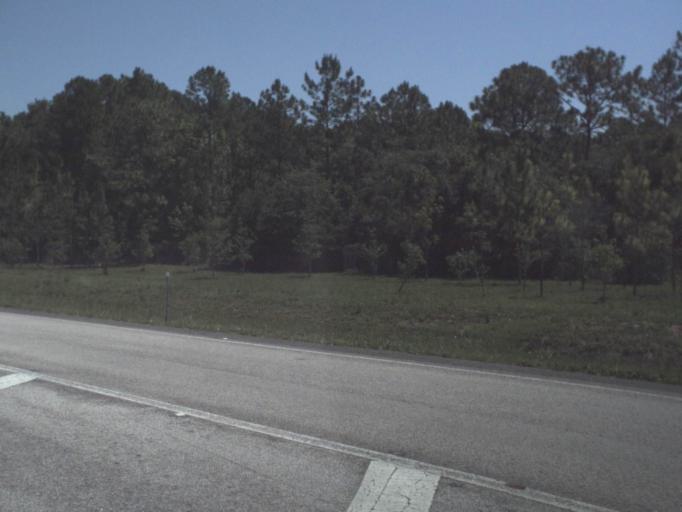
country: US
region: Florida
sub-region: Duval County
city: Jacksonville Beach
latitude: 30.2726
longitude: -81.5211
